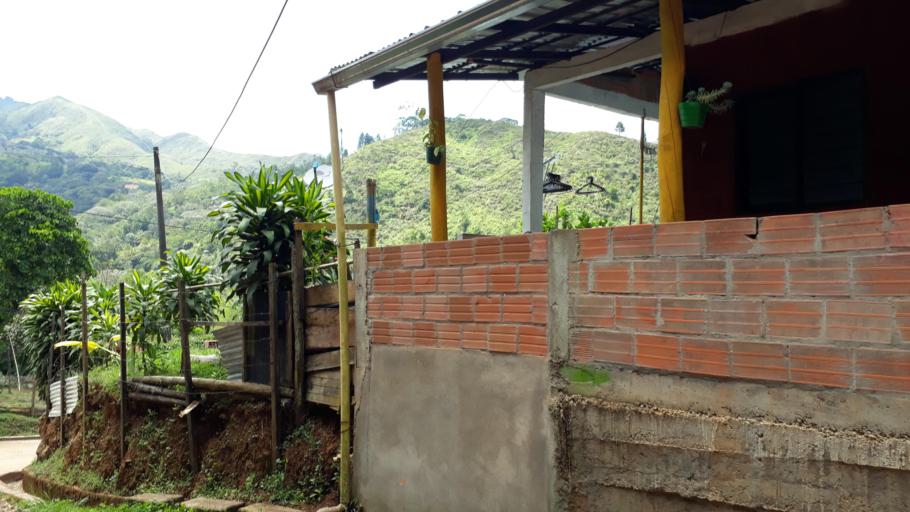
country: CO
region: Valle del Cauca
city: Jamundi
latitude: 3.2719
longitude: -76.6171
